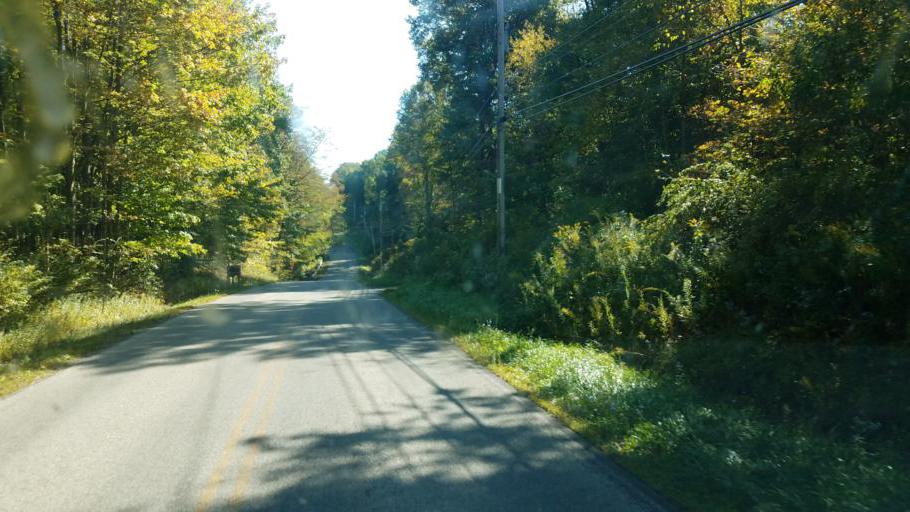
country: US
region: Ohio
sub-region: Richland County
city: Lexington
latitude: 40.6805
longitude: -82.6210
